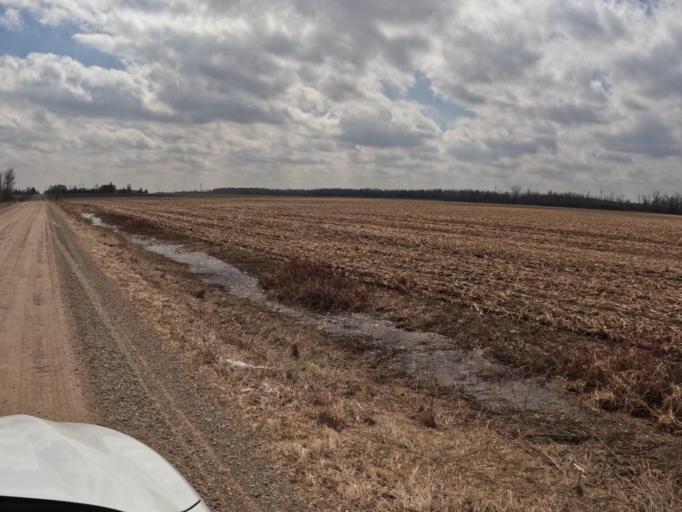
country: CA
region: Ontario
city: Shelburne
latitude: 44.0260
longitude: -80.3310
